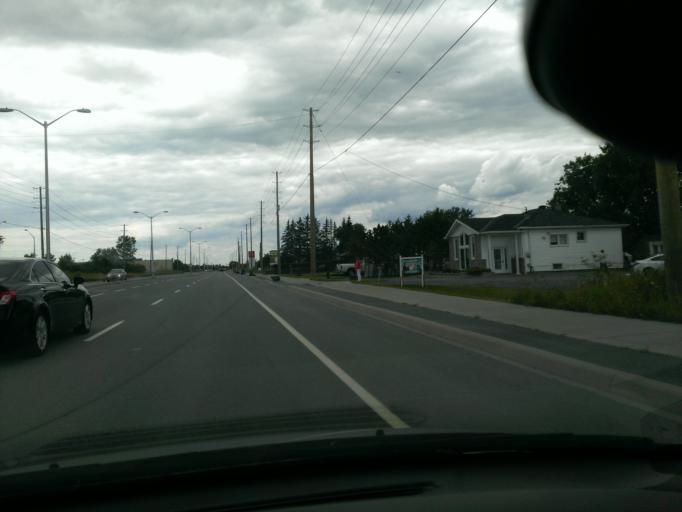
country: CA
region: Ontario
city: Ottawa
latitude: 45.4500
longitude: -75.5012
